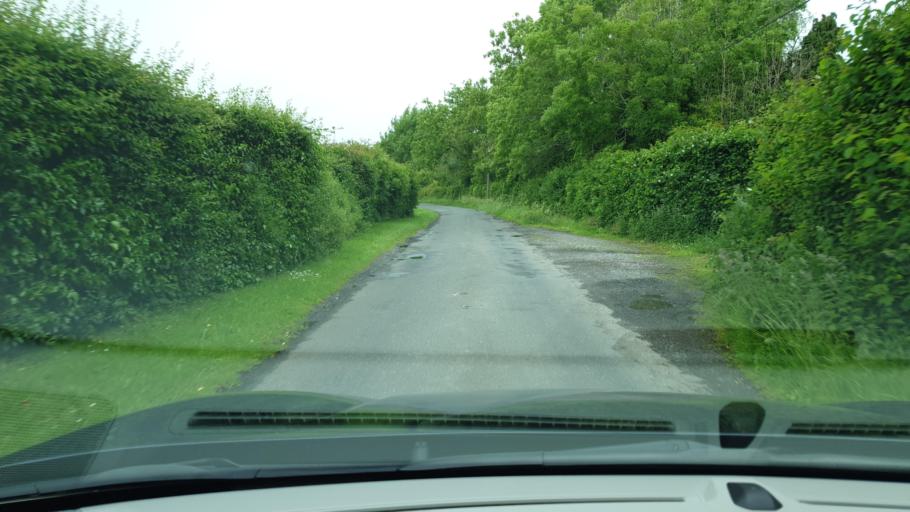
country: IE
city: Confey
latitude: 53.4116
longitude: -6.5262
